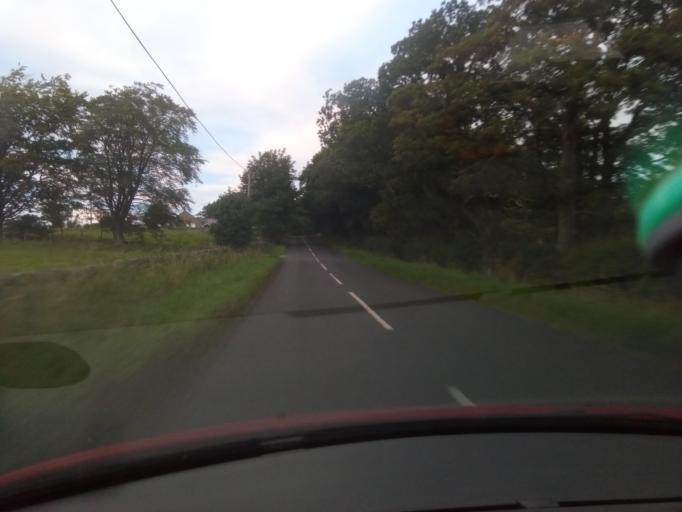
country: GB
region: England
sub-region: Northumberland
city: Bardon Mill
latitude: 54.9227
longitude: -2.3492
